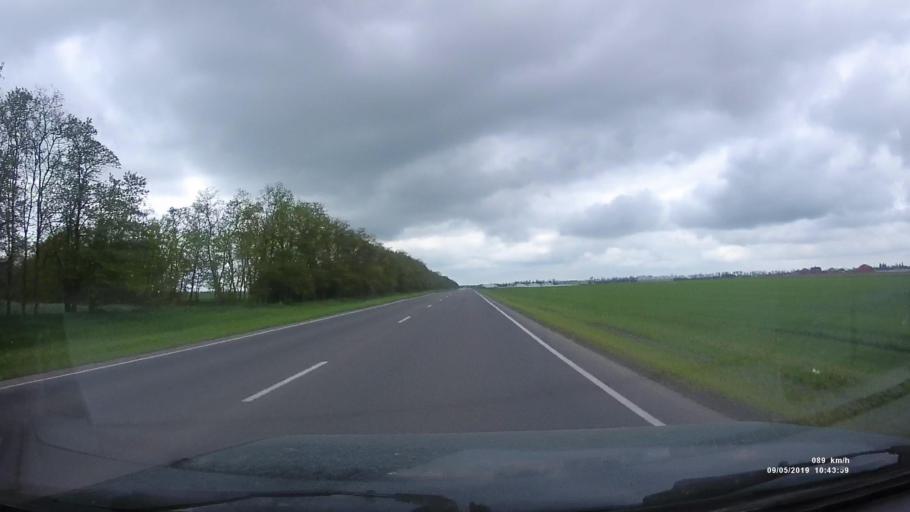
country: RU
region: Rostov
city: Peshkovo
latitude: 47.0040
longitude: 39.3954
